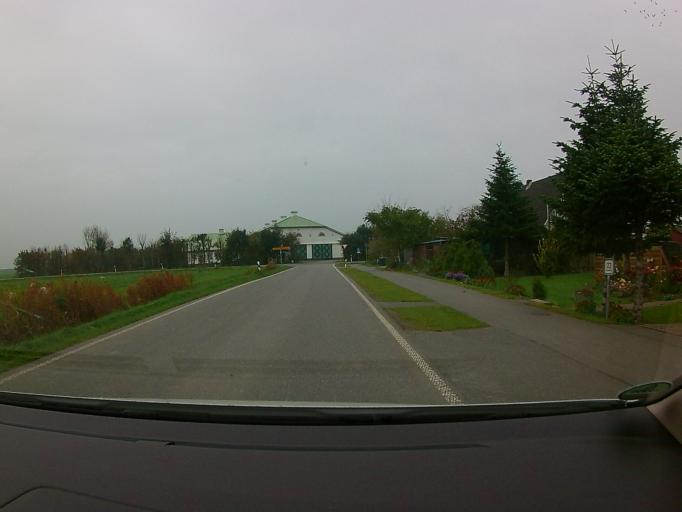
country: DE
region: Schleswig-Holstein
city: Reussenkoge
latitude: 54.6206
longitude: 8.8840
